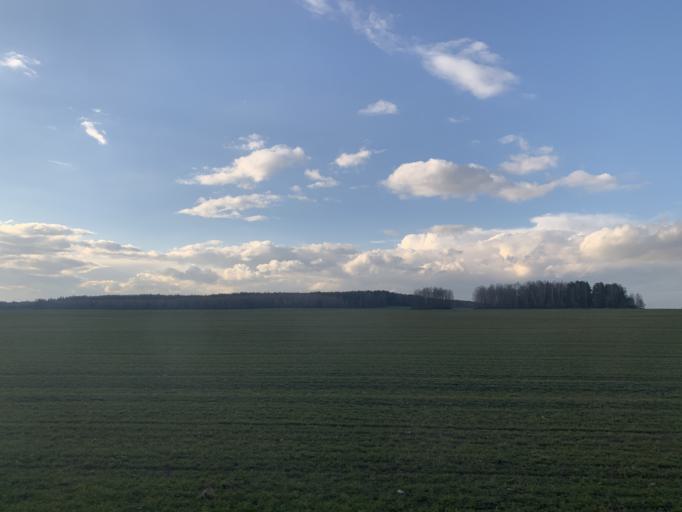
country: BY
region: Minsk
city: Novy Svyerzhan'
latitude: 53.3744
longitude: 26.7145
